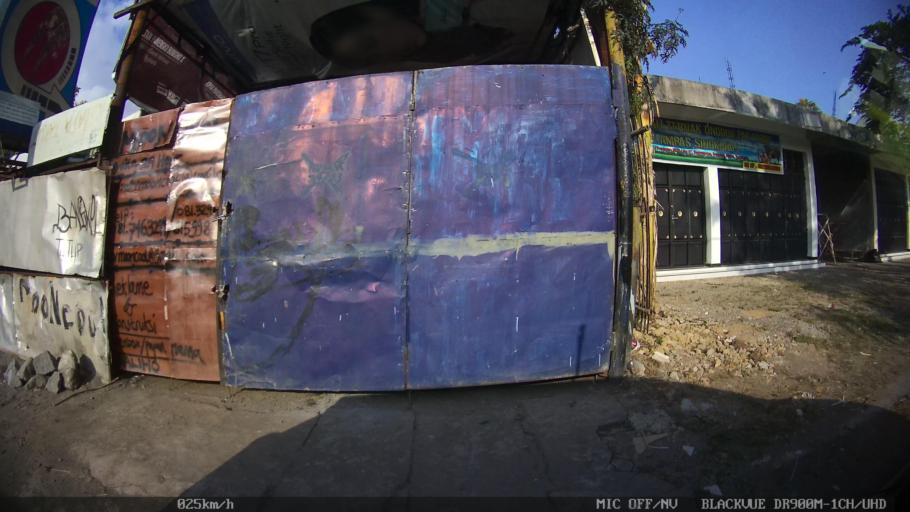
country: ID
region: Daerah Istimewa Yogyakarta
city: Gamping Lor
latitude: -7.7923
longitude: 110.3335
